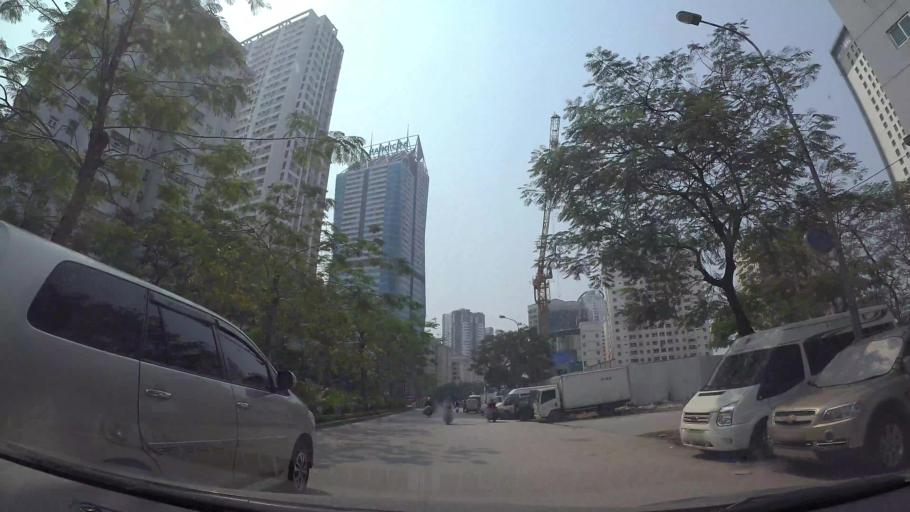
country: VN
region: Ha Noi
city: Thanh Xuan
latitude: 21.0045
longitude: 105.8059
